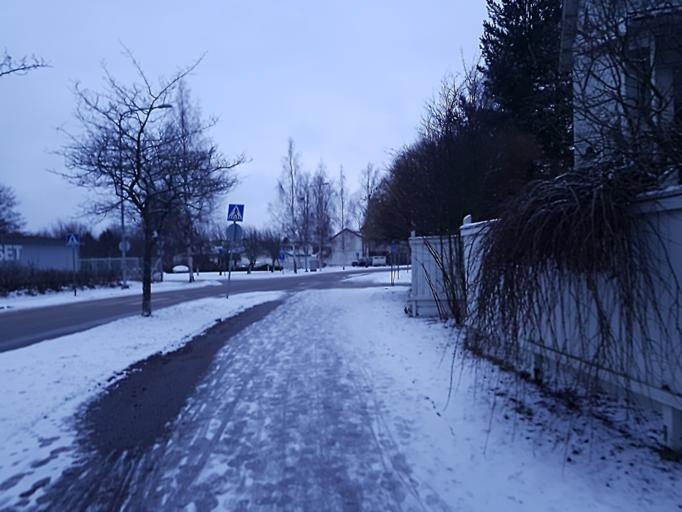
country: FI
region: Uusimaa
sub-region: Helsinki
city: Helsinki
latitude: 60.2585
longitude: 24.9442
